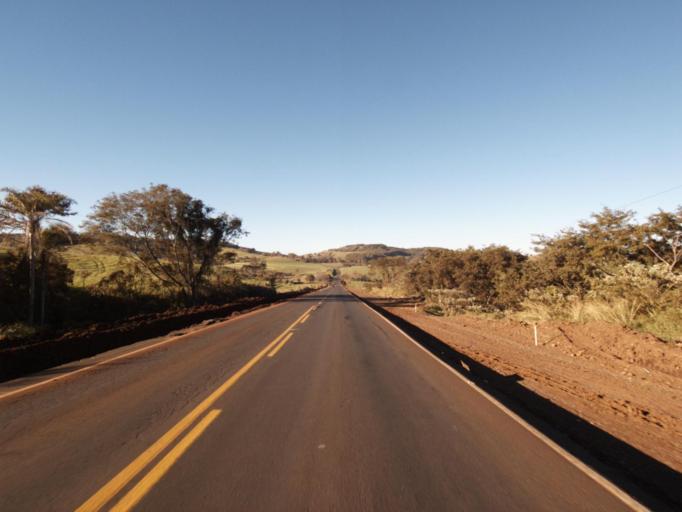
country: AR
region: Misiones
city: Bernardo de Irigoyen
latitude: -26.3612
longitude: -53.5352
